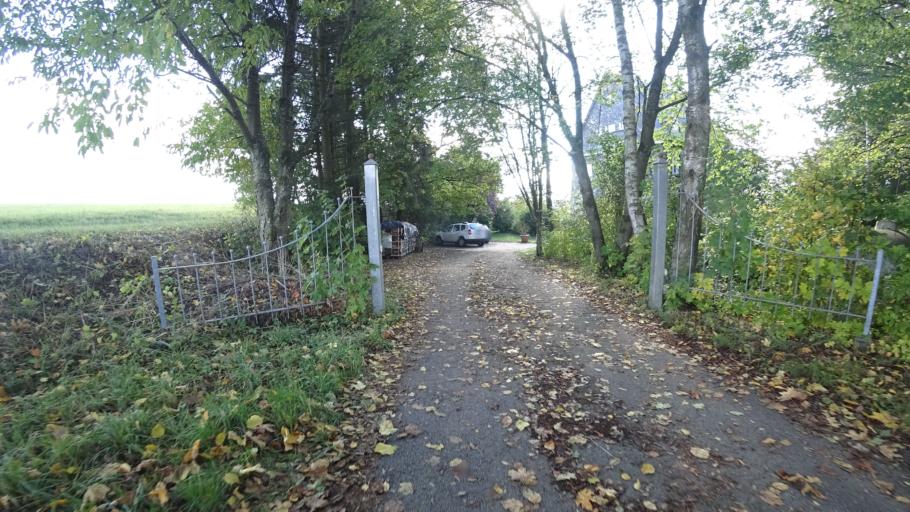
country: DE
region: Rheinland-Pfalz
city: Reich
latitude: 50.0058
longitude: 7.4317
